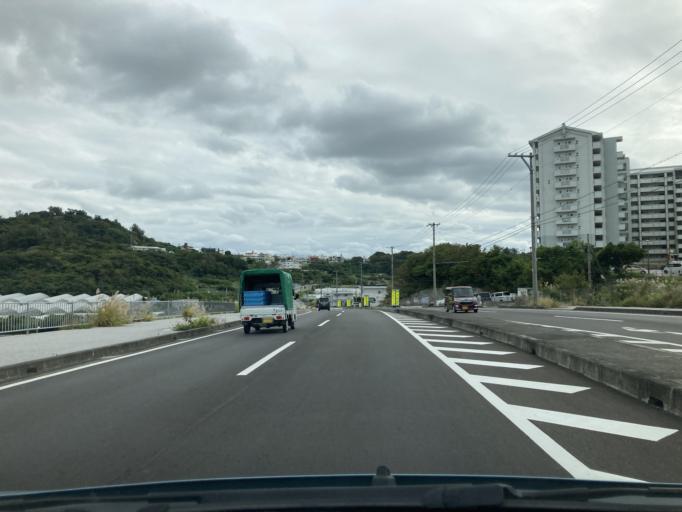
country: JP
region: Okinawa
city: Tomigusuku
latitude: 26.1680
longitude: 127.6774
